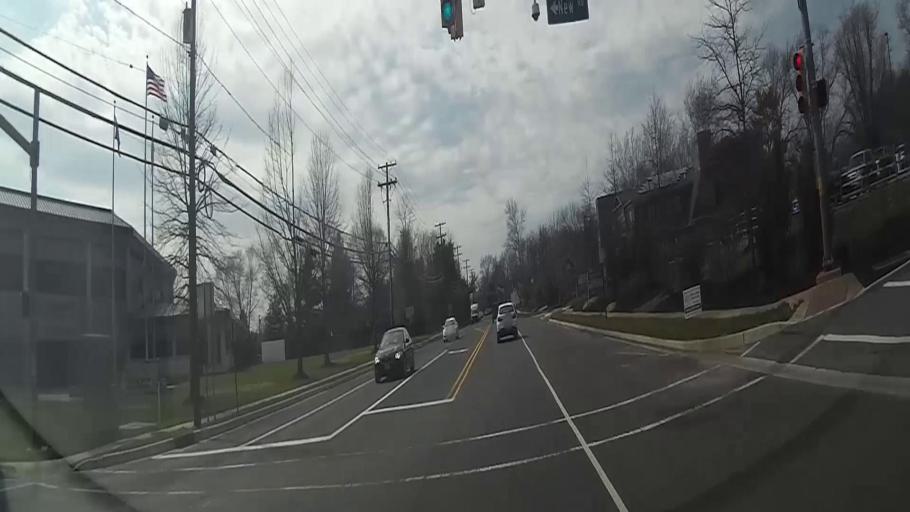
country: US
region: New Jersey
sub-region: Burlington County
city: Marlton
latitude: 39.8831
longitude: -74.8766
